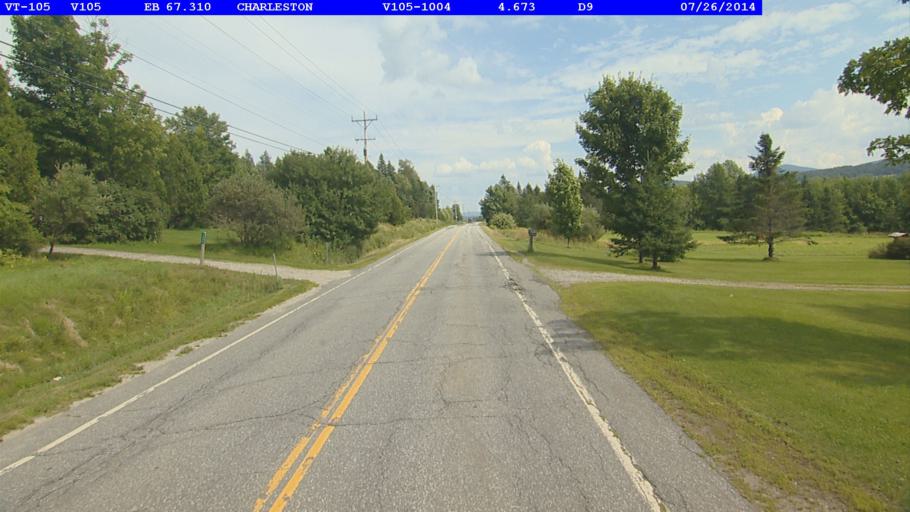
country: US
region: Vermont
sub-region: Orleans County
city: Newport
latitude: 44.8541
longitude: -72.0319
